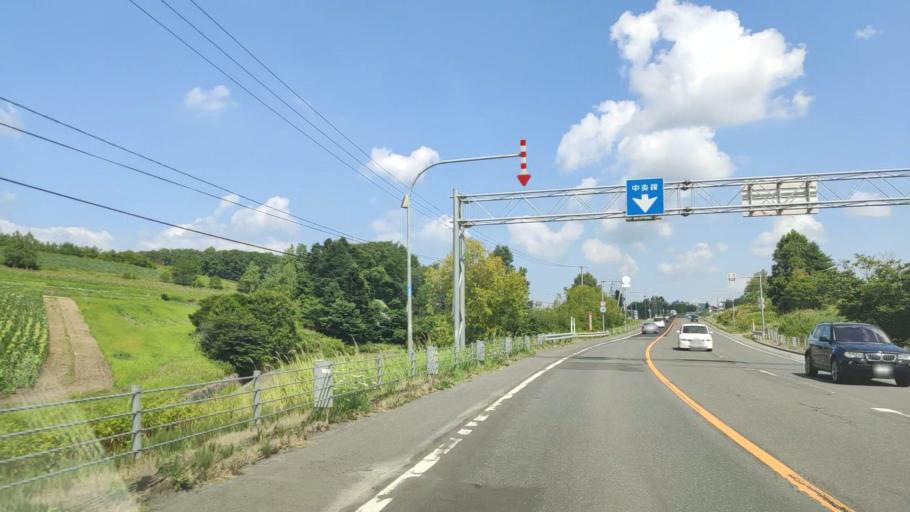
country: JP
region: Hokkaido
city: Shimo-furano
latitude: 43.5374
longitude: 142.4394
